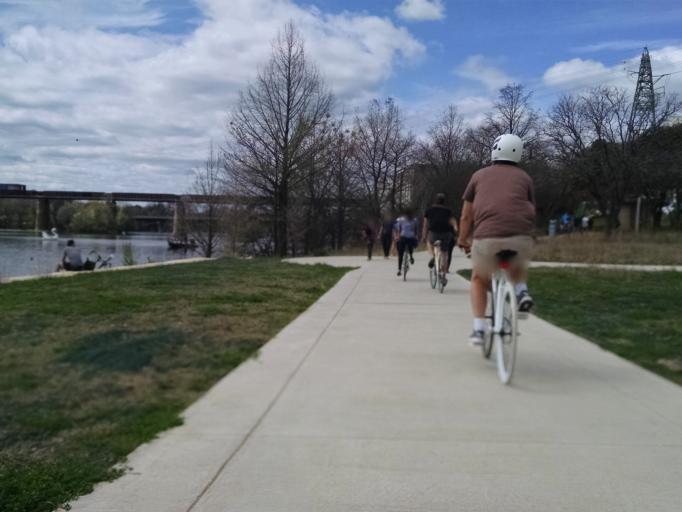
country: US
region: Texas
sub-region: Travis County
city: Austin
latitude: 30.2646
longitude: -97.7513
